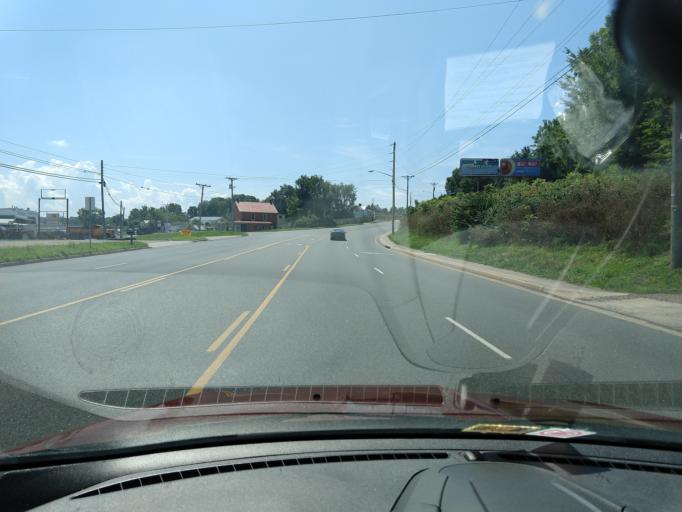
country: US
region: Virginia
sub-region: City of Harrisonburg
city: Harrisonburg
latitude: 38.4633
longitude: -78.8698
